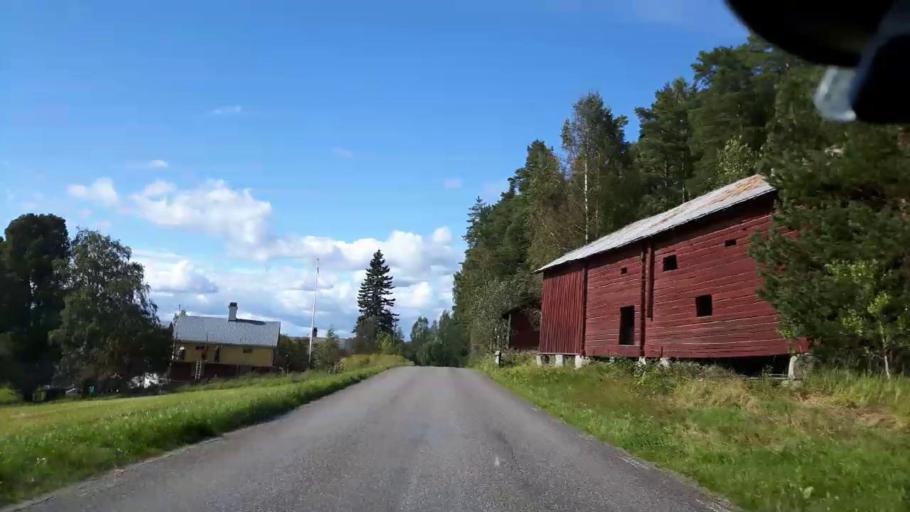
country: SE
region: Jaemtland
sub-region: Braecke Kommun
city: Braecke
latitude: 63.1720
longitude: 15.5695
